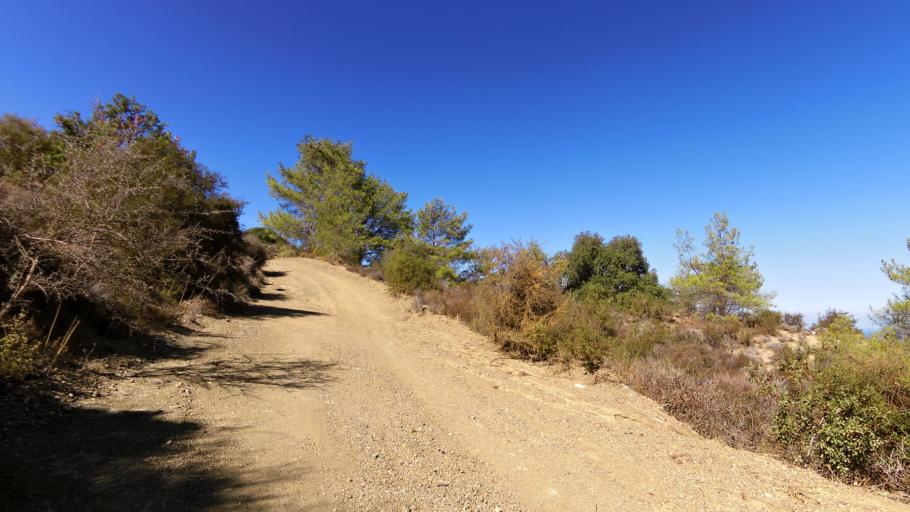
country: CY
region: Pafos
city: Polis
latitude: 35.0132
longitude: 32.4872
